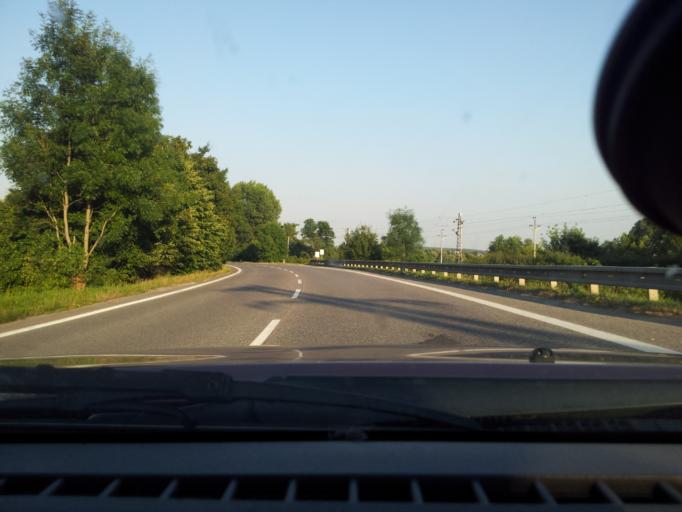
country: SK
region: Trnavsky
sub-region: Okres Skalica
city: Holic
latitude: 48.8205
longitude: 17.1424
